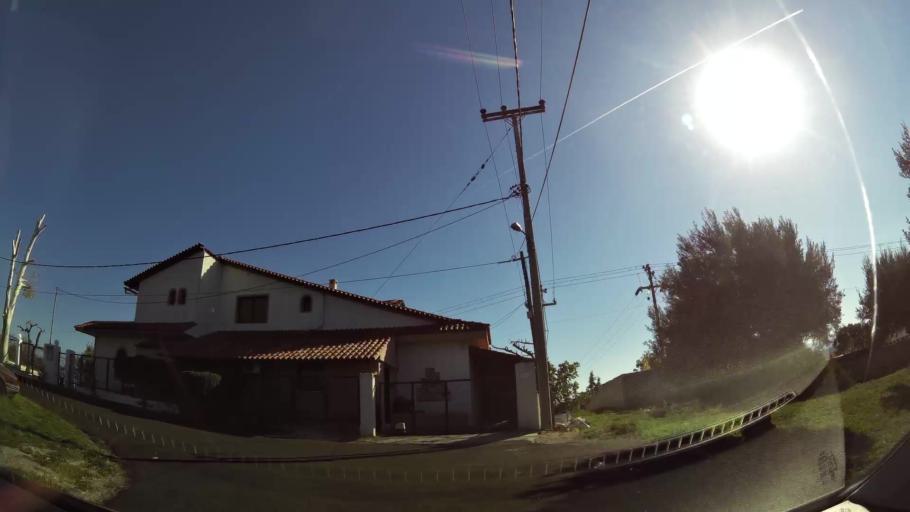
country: GR
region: Attica
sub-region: Nomarchia Anatolikis Attikis
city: Dhrafi
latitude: 38.0050
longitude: 23.9032
